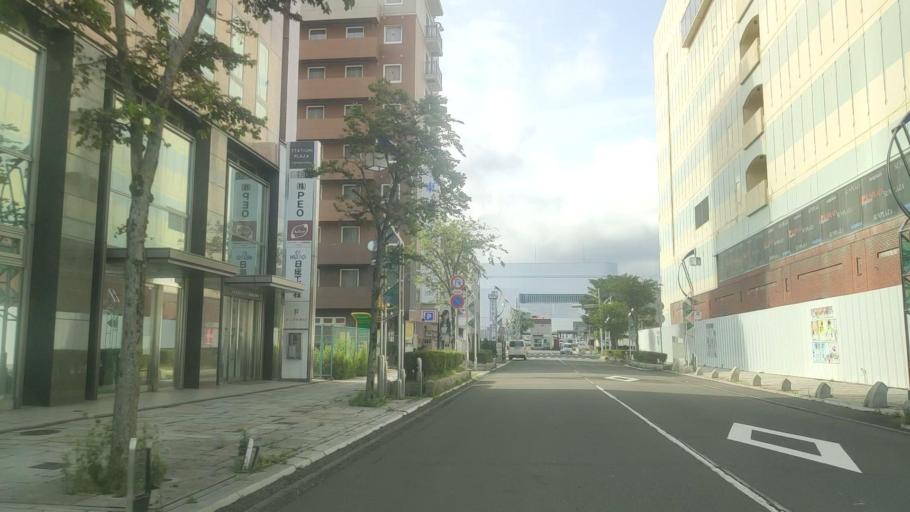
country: JP
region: Hokkaido
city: Tomakomai
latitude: 42.6380
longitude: 141.5973
